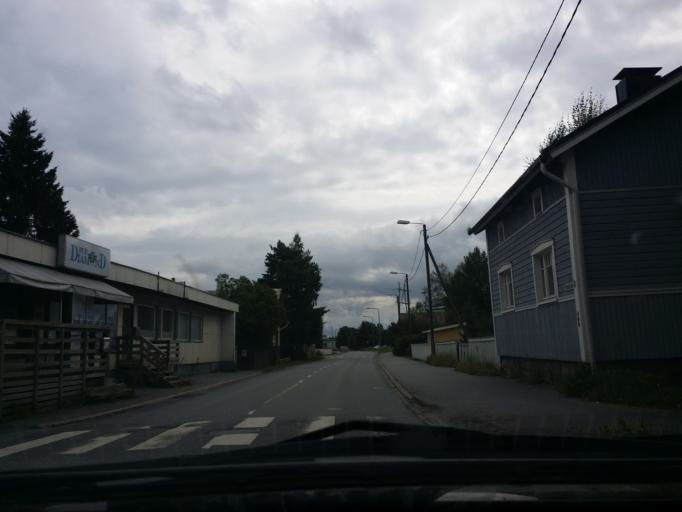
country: FI
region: Satakunta
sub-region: Pori
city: Pori
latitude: 61.5008
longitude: 21.8037
